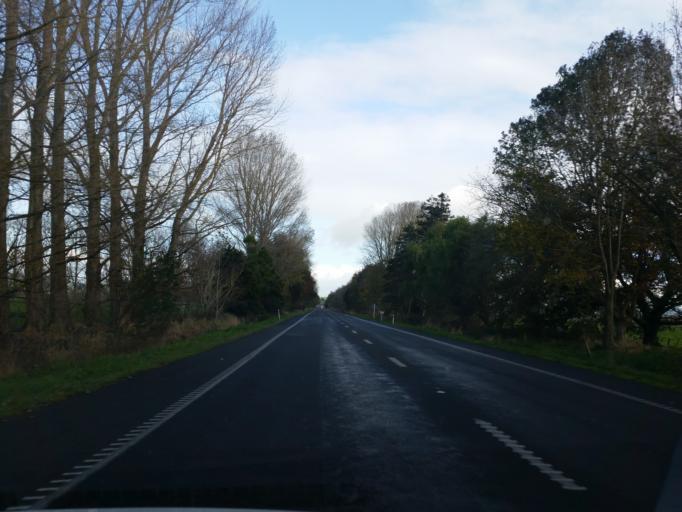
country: NZ
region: Waikato
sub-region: Hauraki District
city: Ngatea
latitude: -37.2797
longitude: 175.4376
